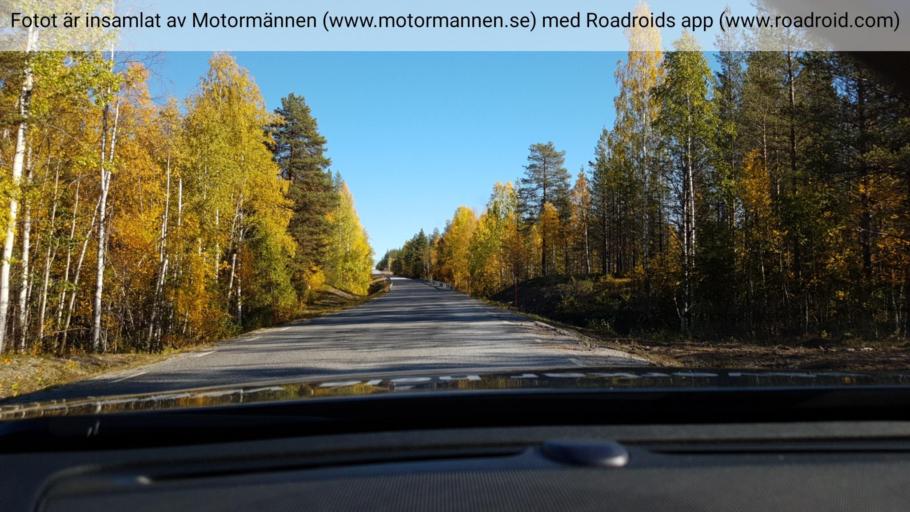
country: SE
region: Norrbotten
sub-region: Gallivare Kommun
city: Gaellivare
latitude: 66.4677
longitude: 20.8336
